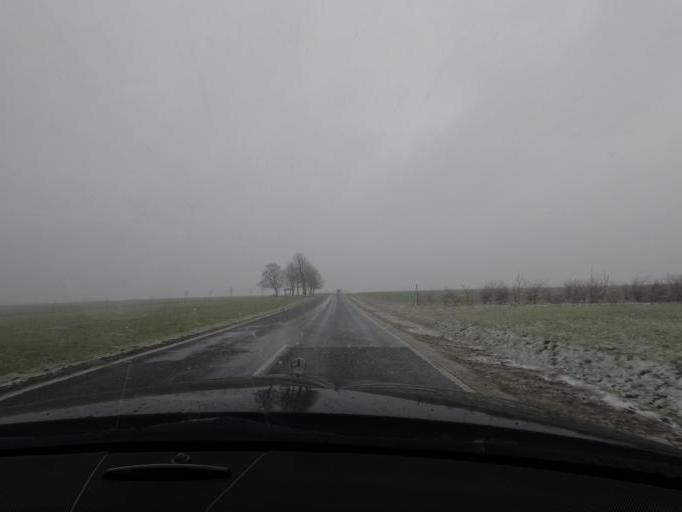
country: DE
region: Thuringia
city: Kullstedt
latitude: 51.2624
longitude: 10.2759
